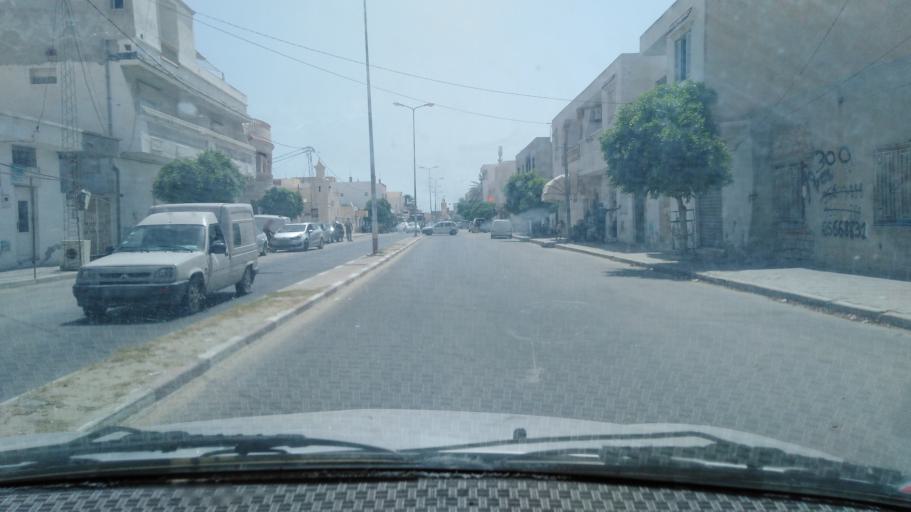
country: TN
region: Qabis
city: Gabes
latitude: 33.9600
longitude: 9.9985
